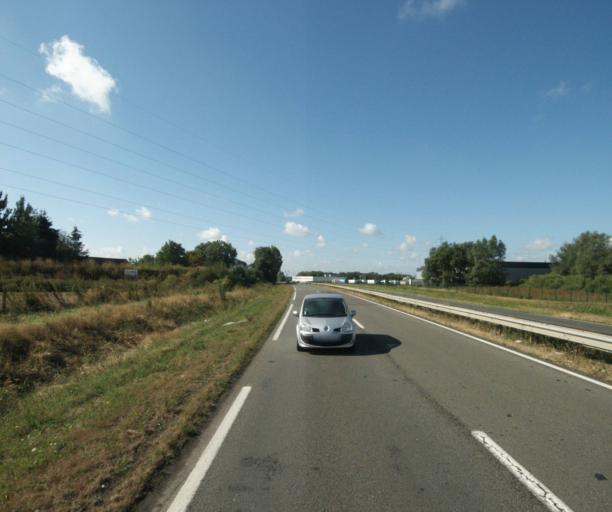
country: FR
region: Nord-Pas-de-Calais
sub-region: Departement du Nord
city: Sailly-lez-Lannoy
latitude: 50.6538
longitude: 3.2085
